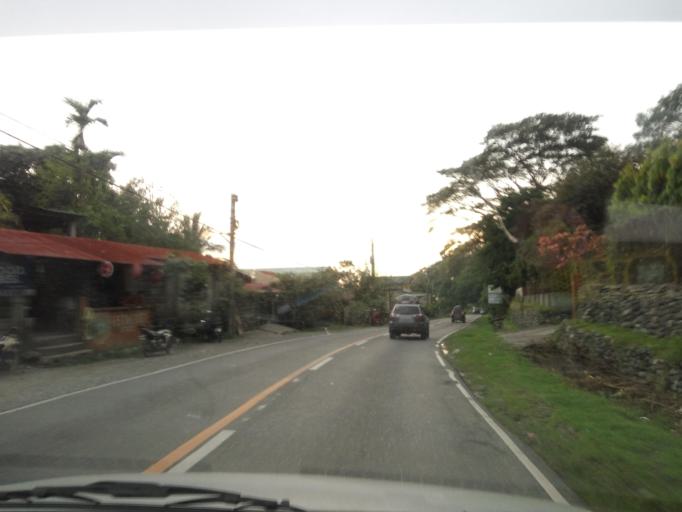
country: PH
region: Ilocos
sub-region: Province of La Union
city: Caronoan West
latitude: 16.2271
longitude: 120.4458
